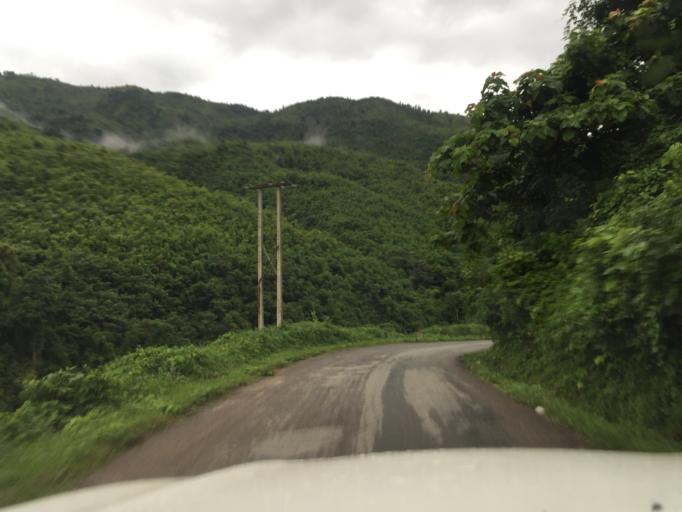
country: LA
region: Oudomxai
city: Muang La
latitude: 20.9628
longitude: 102.2203
